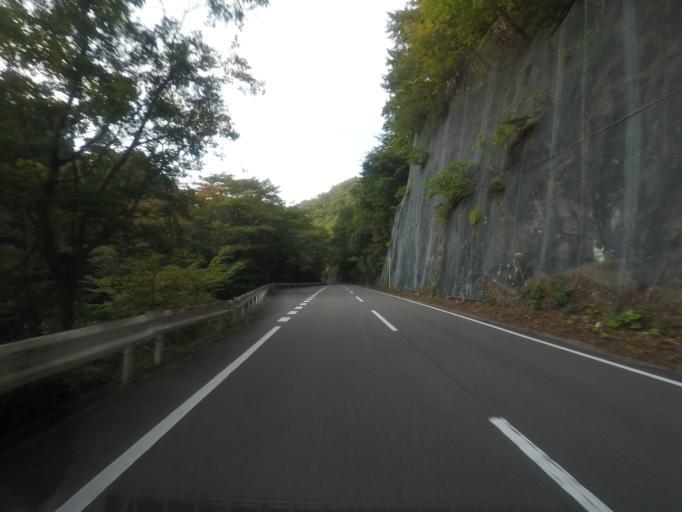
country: JP
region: Fukushima
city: Namie
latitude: 37.5558
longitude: 140.8329
